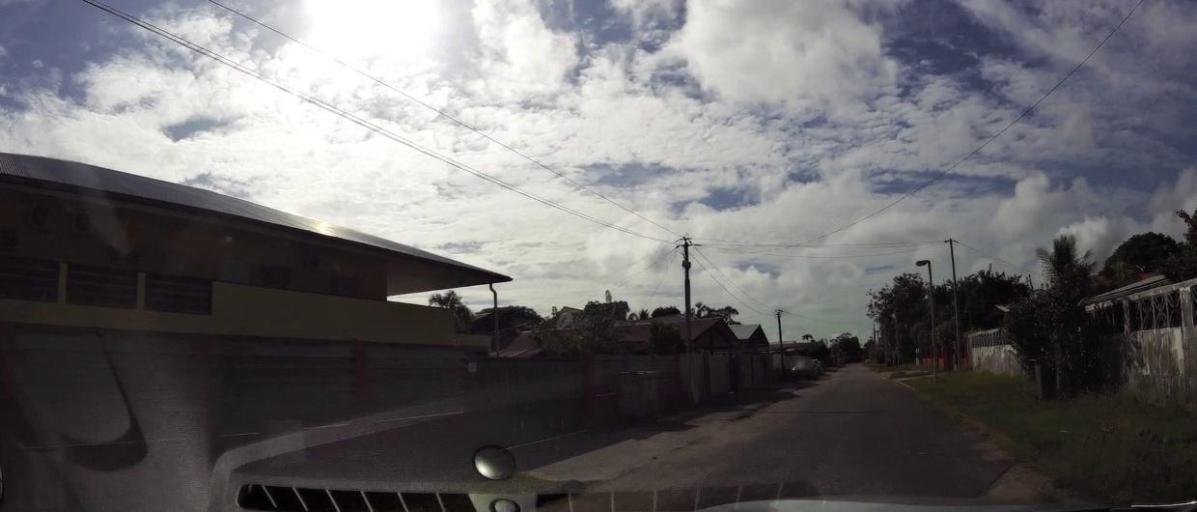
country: GF
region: Guyane
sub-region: Guyane
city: Kourou
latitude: 5.1609
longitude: -52.6421
